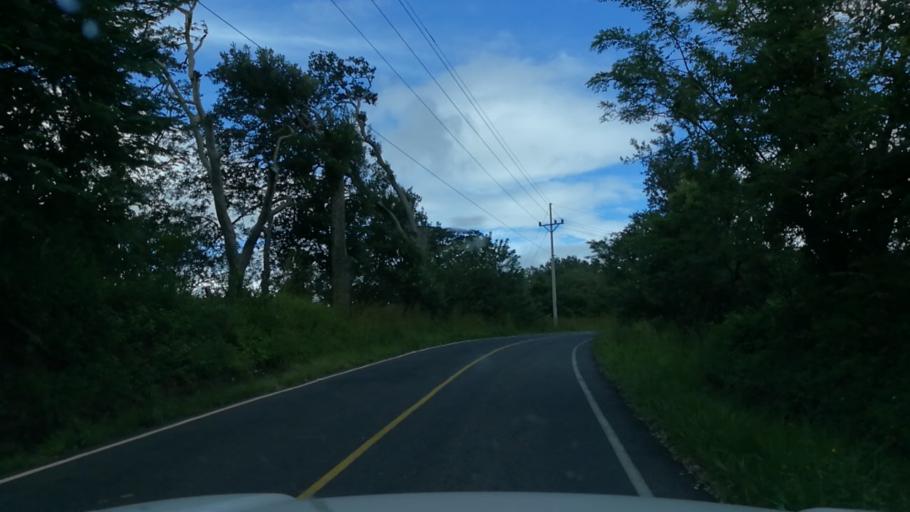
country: CR
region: Guanacaste
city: Fortuna
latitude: 10.6424
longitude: -85.2306
